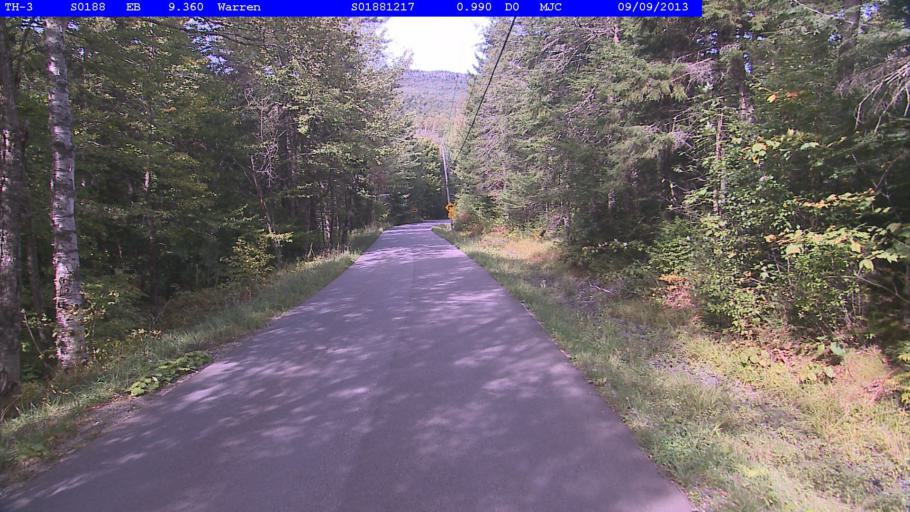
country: US
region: Vermont
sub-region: Addison County
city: Bristol
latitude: 44.0961
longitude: -72.9098
